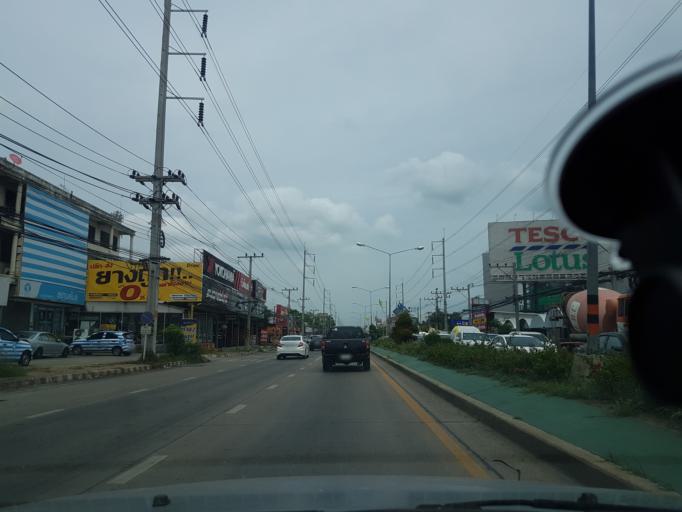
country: TH
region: Lop Buri
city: Lop Buri
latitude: 14.7880
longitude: 100.6775
